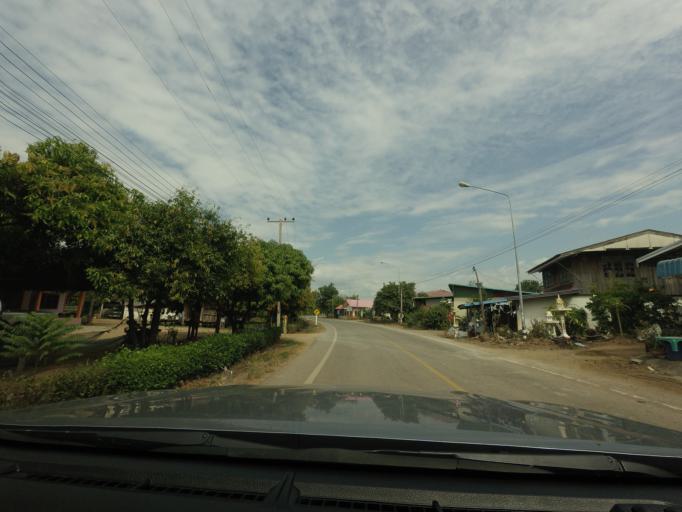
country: TH
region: Phitsanulok
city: Wang Thong
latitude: 16.7299
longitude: 100.3778
